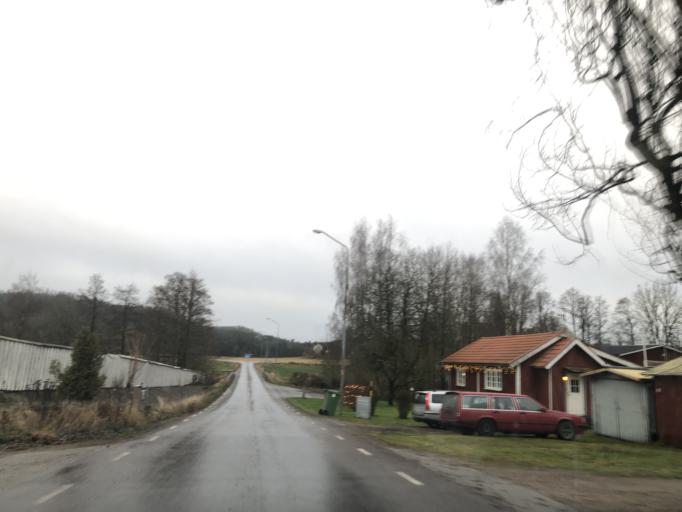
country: SE
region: Vaestra Goetaland
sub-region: Ulricehamns Kommun
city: Ulricehamn
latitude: 57.8001
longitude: 13.3713
